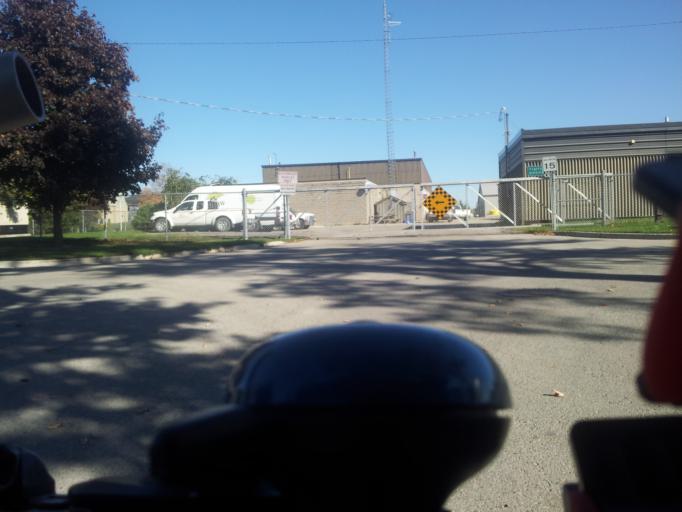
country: CA
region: Ontario
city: Stratford
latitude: 43.3650
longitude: -80.9670
